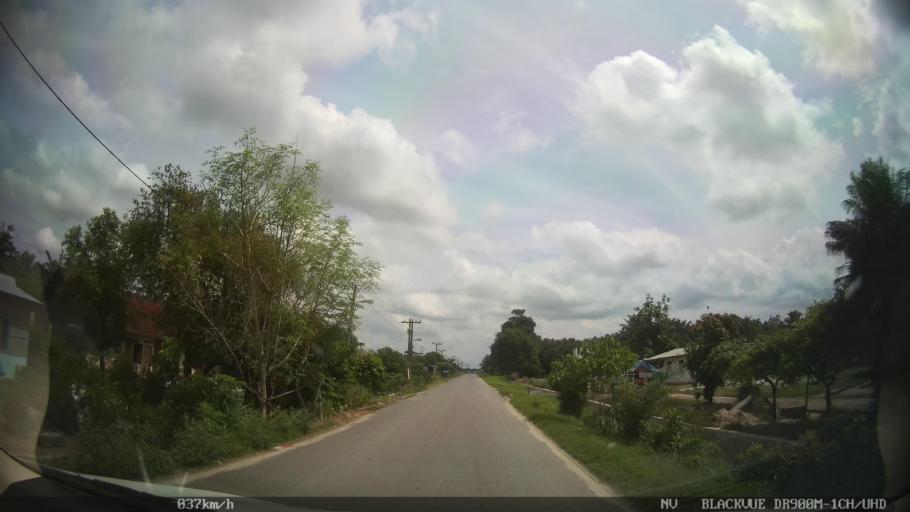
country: ID
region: North Sumatra
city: Percut
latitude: 3.5933
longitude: 98.8401
